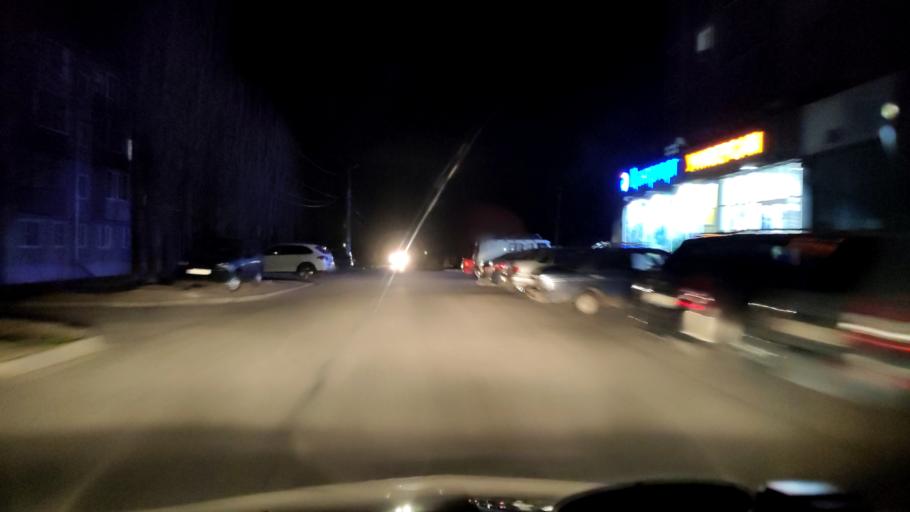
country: RU
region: Voronezj
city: Semiluki
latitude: 51.6932
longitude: 39.0165
